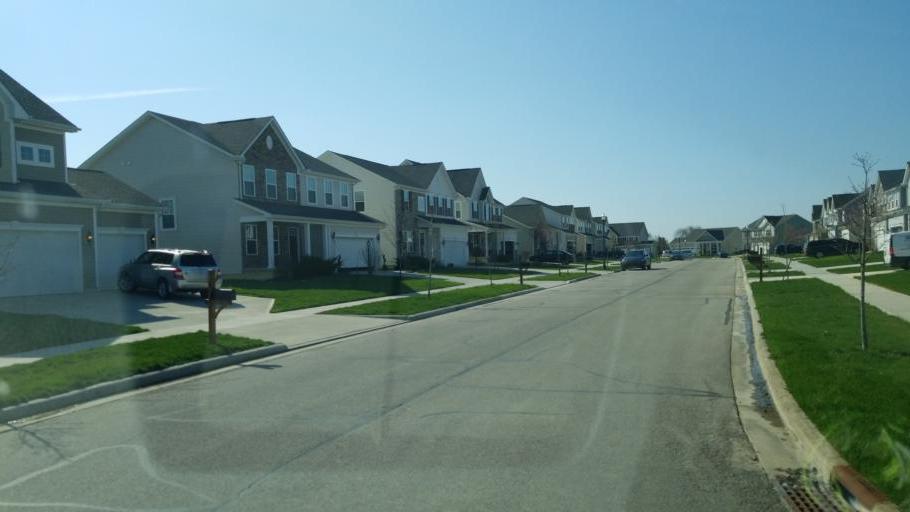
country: US
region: Ohio
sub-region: Delaware County
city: Delaware
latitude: 40.3025
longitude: -83.0395
